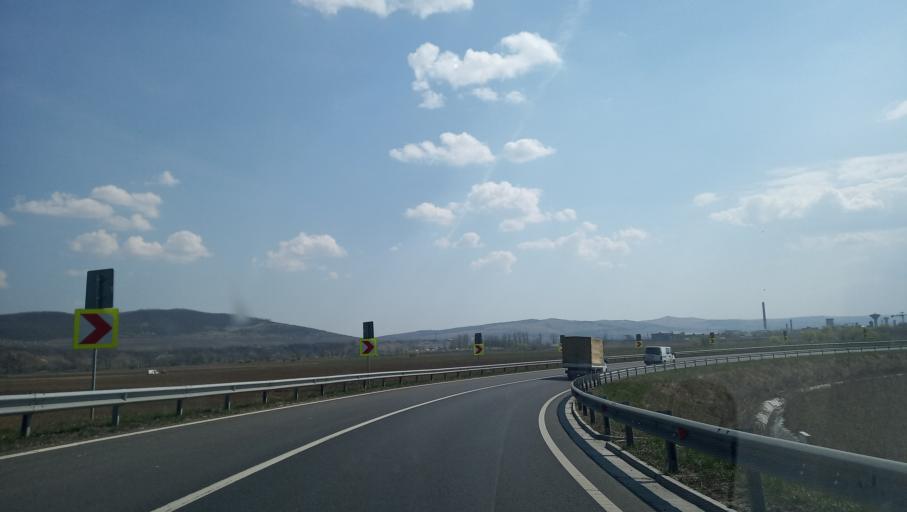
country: RO
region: Alba
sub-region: Municipiul Aiud
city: Aiud
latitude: 46.3294
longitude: 23.7322
